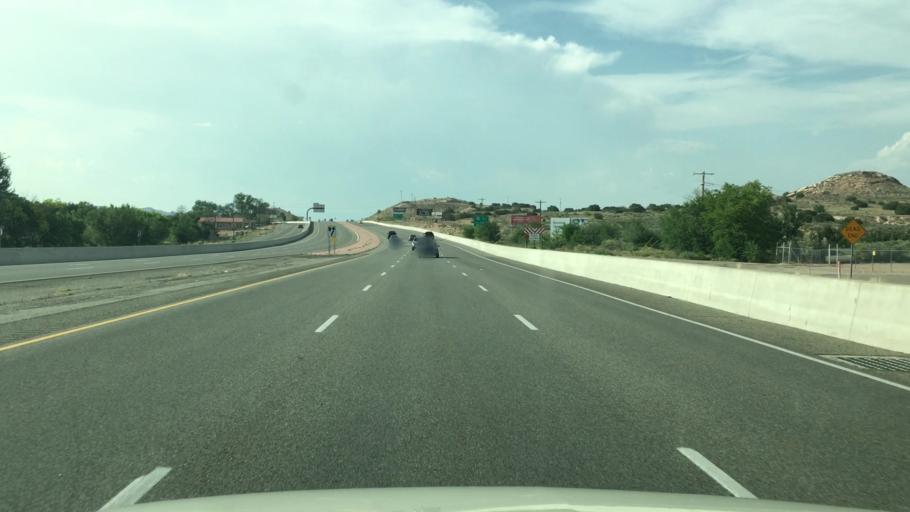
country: US
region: New Mexico
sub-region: Santa Fe County
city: Nambe
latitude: 35.8653
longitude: -106.0017
